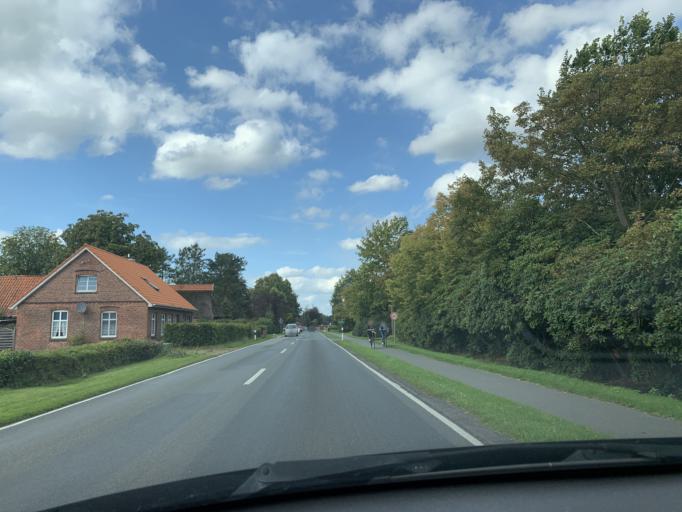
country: DE
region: Lower Saxony
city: Edewecht
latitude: 53.1511
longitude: 7.9994
